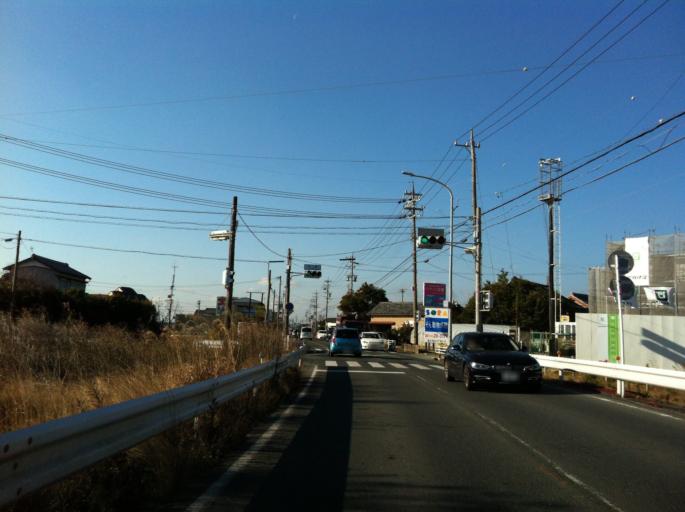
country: JP
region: Aichi
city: Tahara
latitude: 34.6903
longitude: 137.3262
